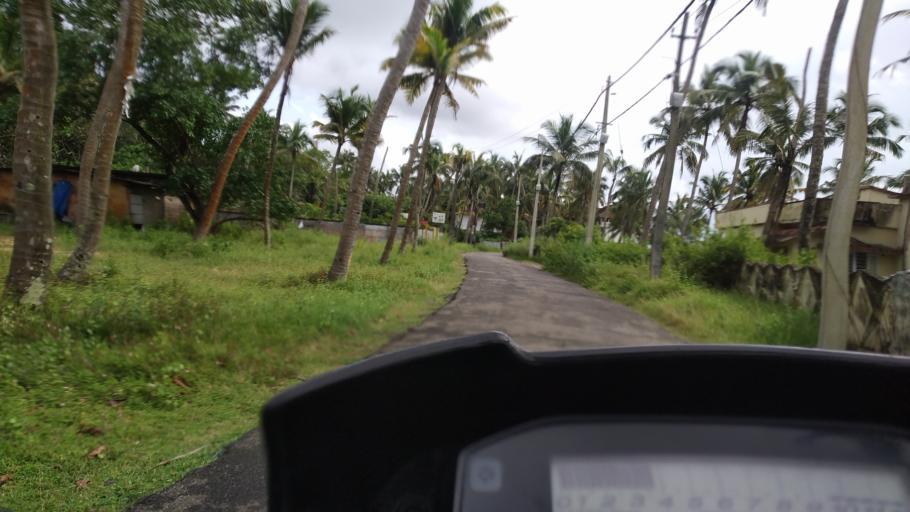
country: IN
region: Kerala
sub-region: Thrissur District
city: Kodungallur
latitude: 10.1645
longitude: 76.1705
